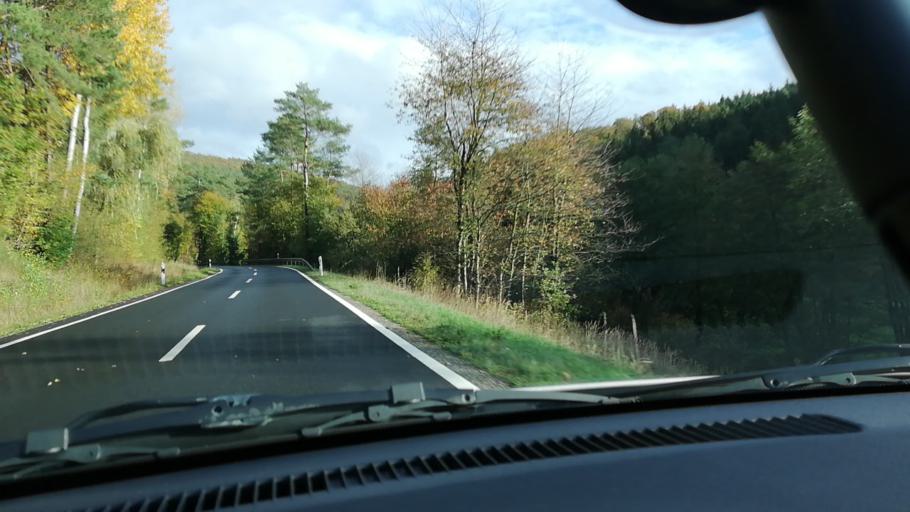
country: DE
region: Bavaria
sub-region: Regierungsbezirk Unterfranken
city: Neuhutten
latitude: 49.9980
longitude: 9.4432
